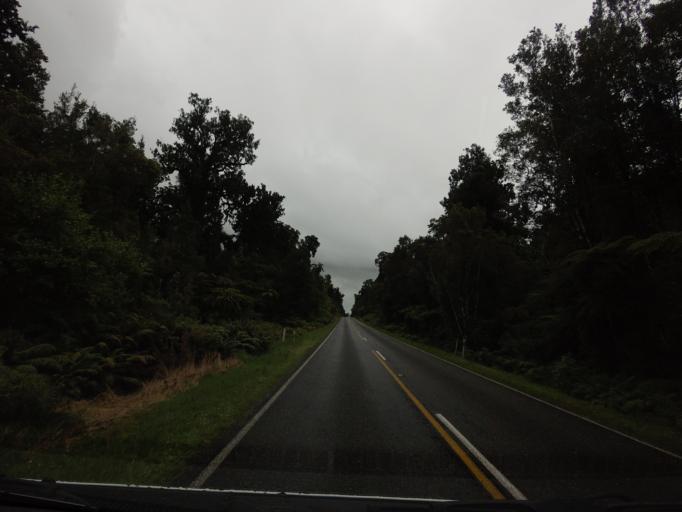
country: NZ
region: West Coast
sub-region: Westland District
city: Hokitika
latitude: -43.0343
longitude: 170.6499
